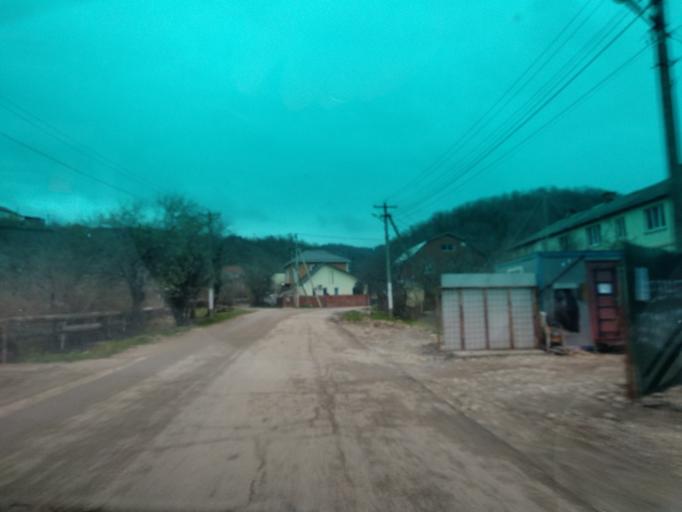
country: RU
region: Krasnodarskiy
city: Novomikhaylovskiy
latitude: 44.2572
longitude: 38.8585
